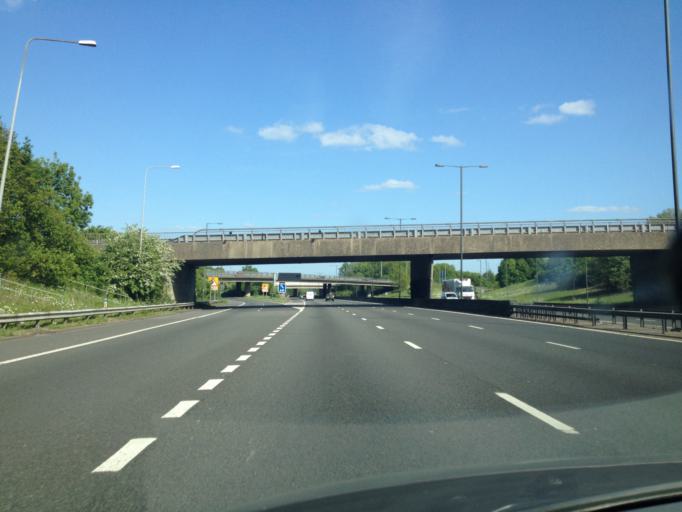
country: GB
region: England
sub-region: Hertfordshire
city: Elstree
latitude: 51.6366
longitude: -0.3059
